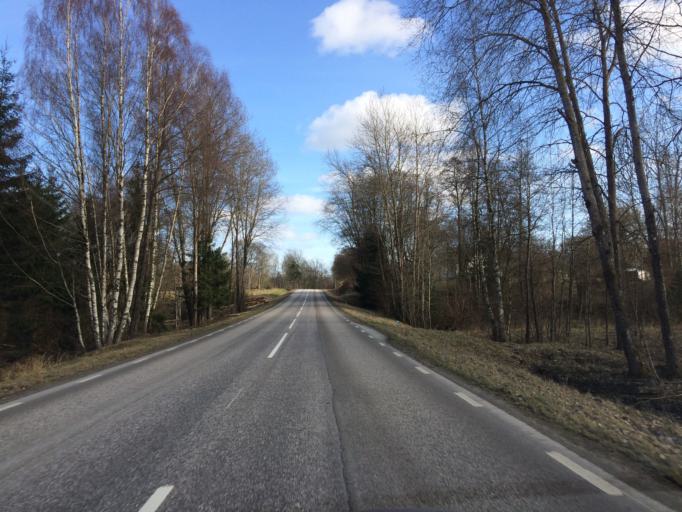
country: SE
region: Kronoberg
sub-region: Almhults Kommun
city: AElmhult
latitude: 56.5751
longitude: 14.1103
